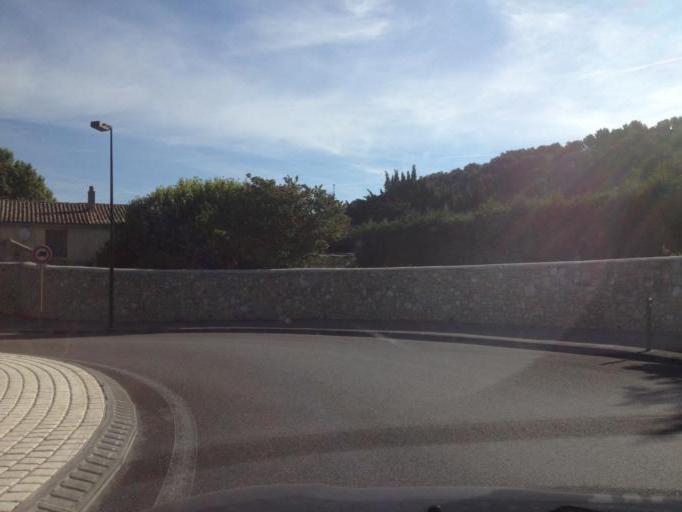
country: FR
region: Provence-Alpes-Cote d'Azur
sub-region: Departement du Vaucluse
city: Orange
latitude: 44.1259
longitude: 4.8012
